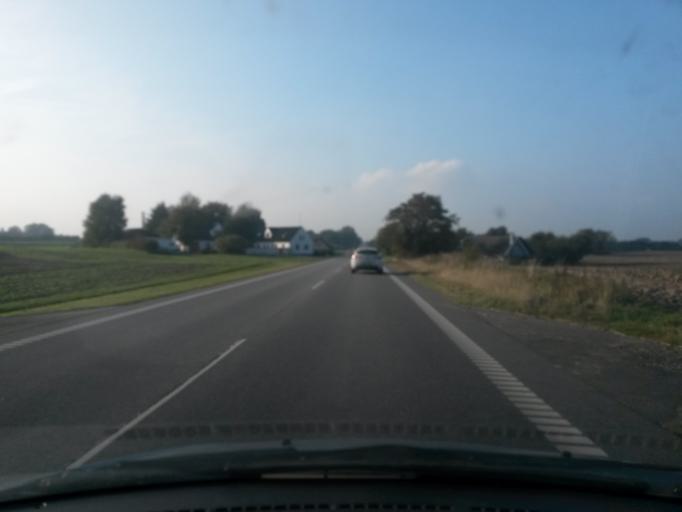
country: DK
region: Central Jutland
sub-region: Syddjurs Kommune
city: Hornslet
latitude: 56.3797
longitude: 10.2993
